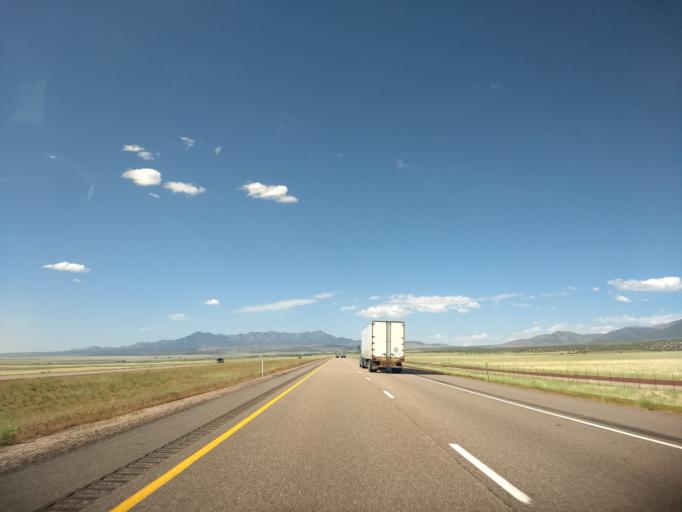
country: US
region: Utah
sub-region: Millard County
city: Fillmore
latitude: 39.0499
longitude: -112.2910
